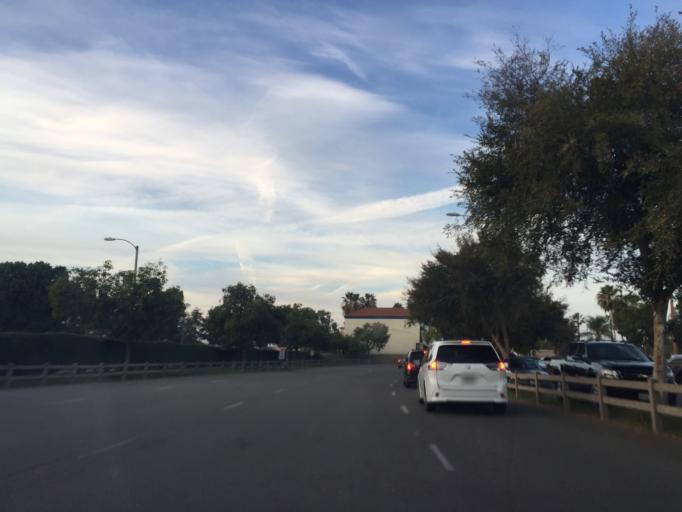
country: US
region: California
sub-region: Orange County
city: Buena Park
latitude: 33.8449
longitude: -117.9974
